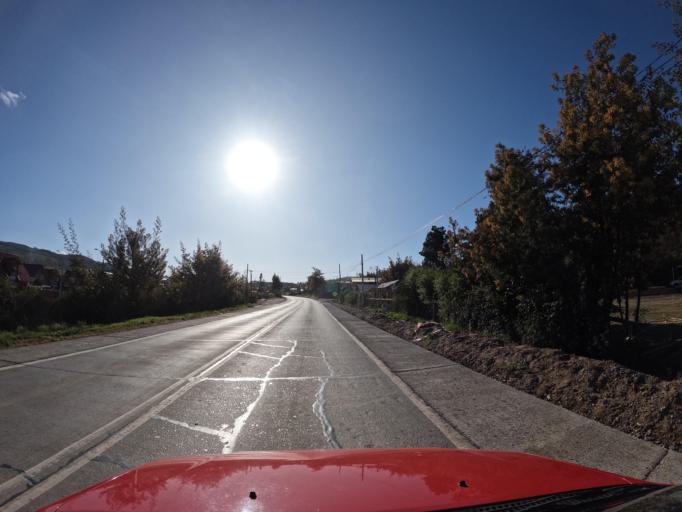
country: CL
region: Maule
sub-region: Provincia de Talca
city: Constitucion
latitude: -35.4543
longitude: -72.2701
